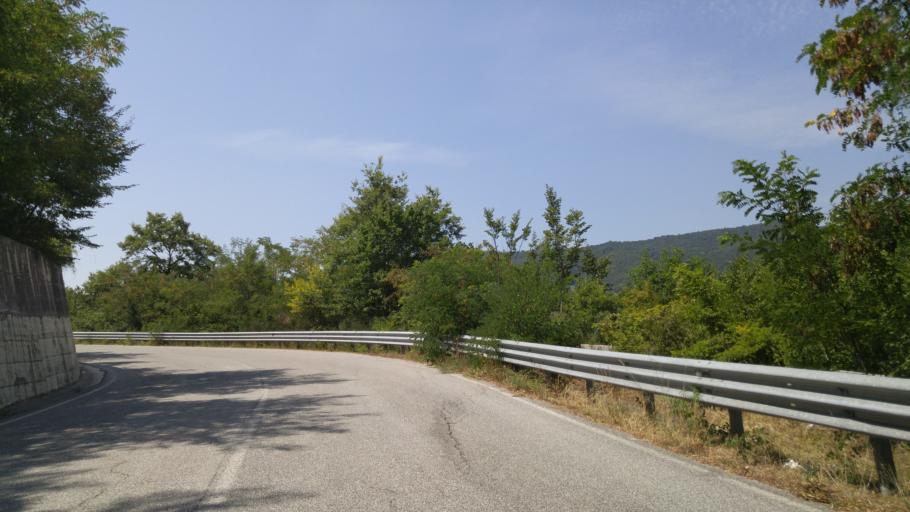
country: IT
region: Umbria
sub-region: Provincia di Perugia
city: Scheggia
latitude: 43.4154
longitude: 12.6547
